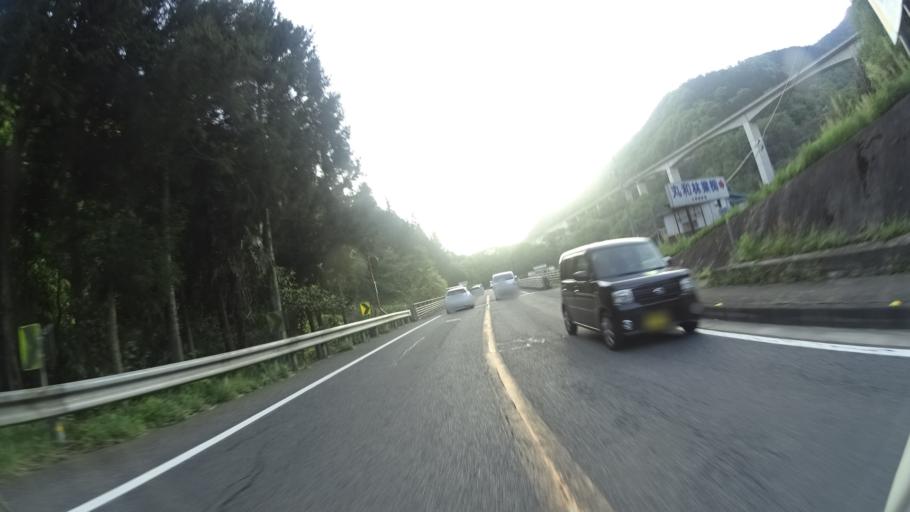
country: JP
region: Tokushima
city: Ikedacho
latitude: 34.0064
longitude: 133.7208
